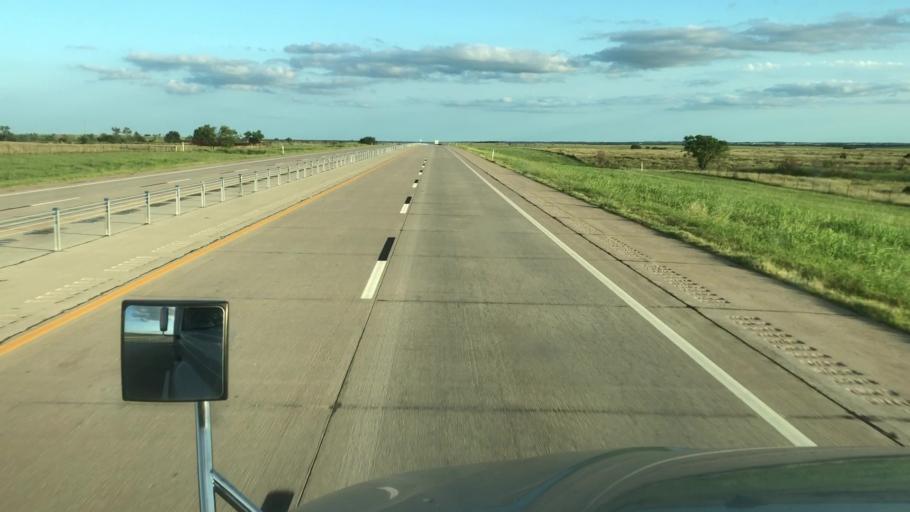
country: US
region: Oklahoma
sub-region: Pawnee County
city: Pawnee
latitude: 36.3645
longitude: -97.0344
